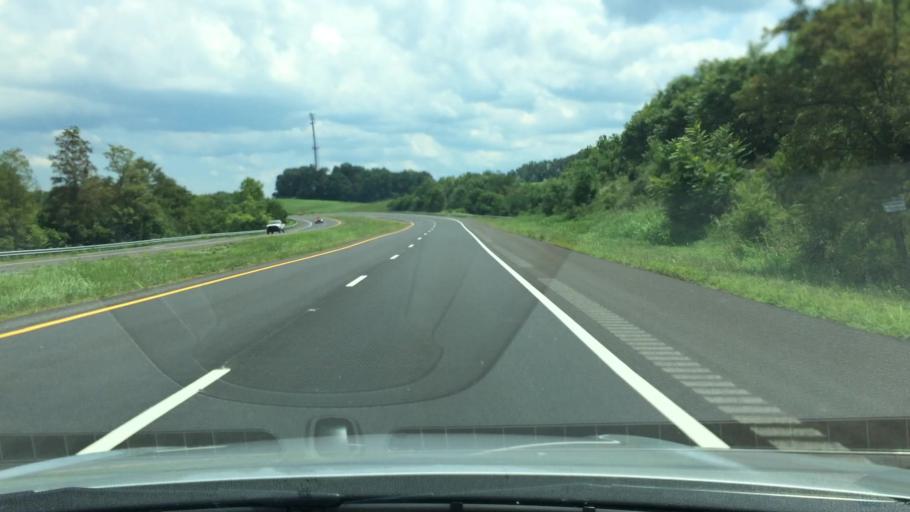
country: US
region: Tennessee
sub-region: Hamblen County
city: Morristown
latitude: 36.1747
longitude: -83.2313
